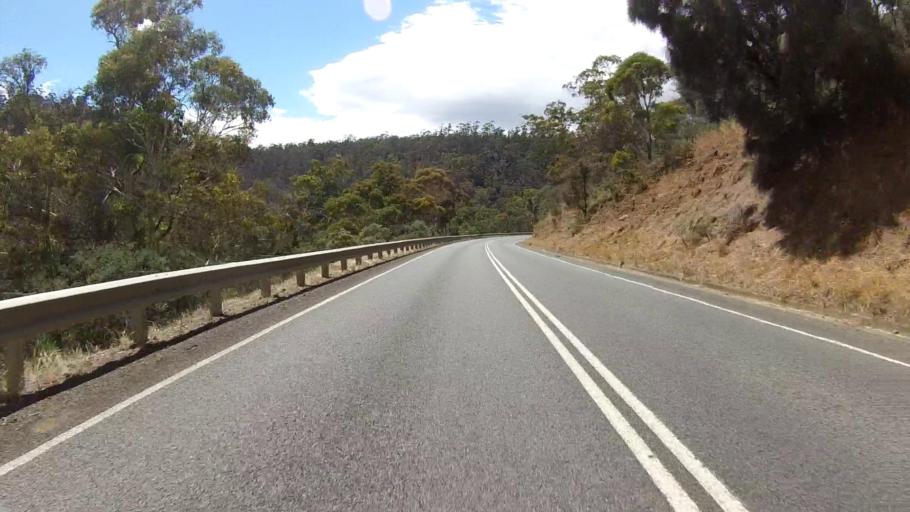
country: AU
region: Tasmania
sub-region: Sorell
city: Sorell
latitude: -42.6068
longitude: 147.6502
